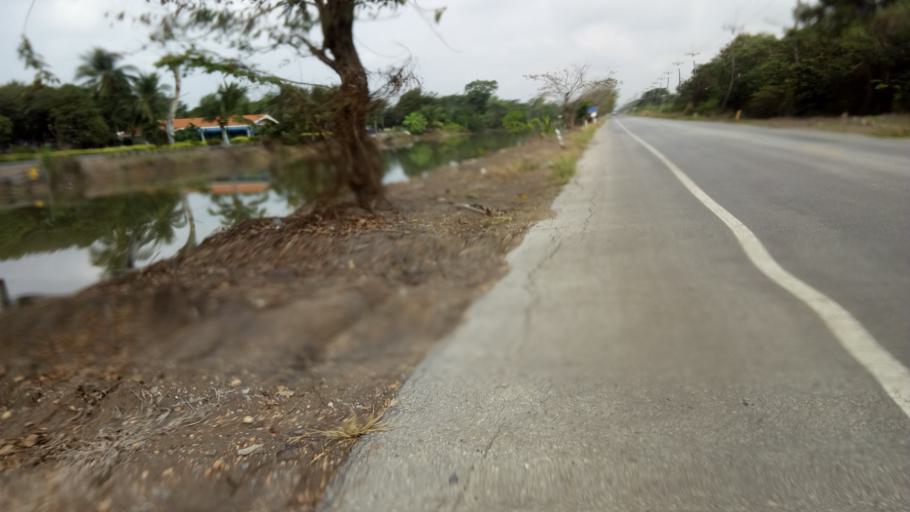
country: TH
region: Pathum Thani
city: Nong Suea
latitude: 14.1638
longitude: 100.8236
